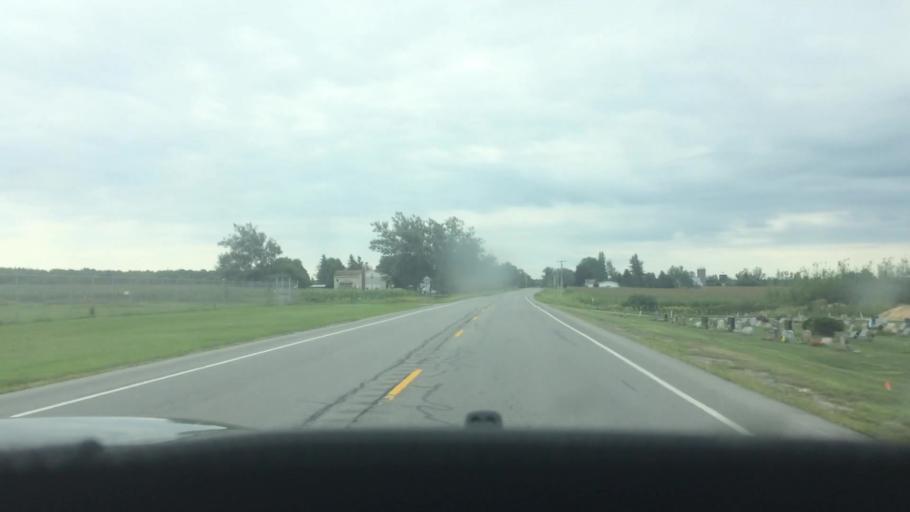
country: US
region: New York
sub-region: St. Lawrence County
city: Ogdensburg
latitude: 44.6770
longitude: -75.4763
